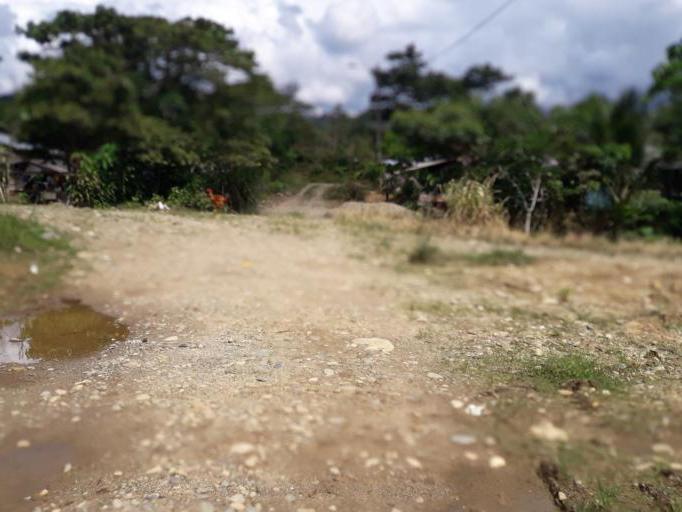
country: EC
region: Napo
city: Tena
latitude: -0.9579
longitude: -77.8164
